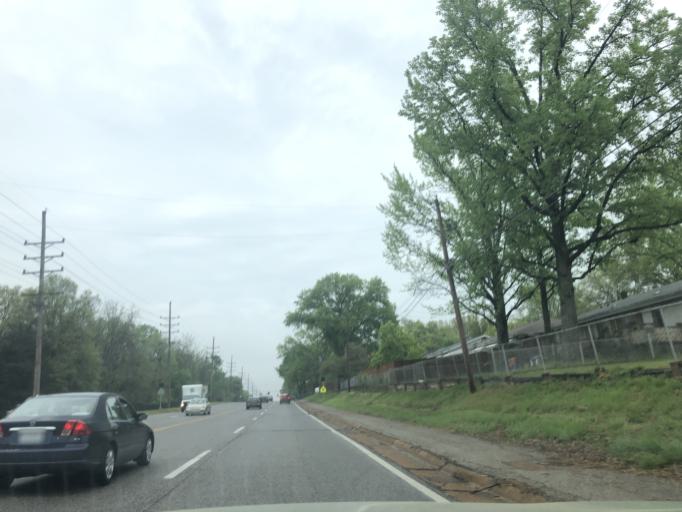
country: US
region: Missouri
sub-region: Saint Louis County
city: Marlborough
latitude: 38.5705
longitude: -90.3199
